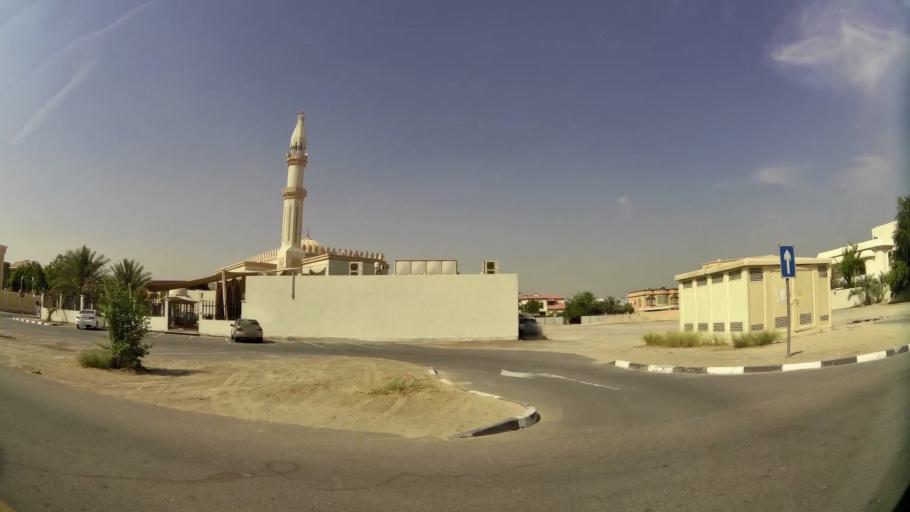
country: AE
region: Ash Shariqah
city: Sharjah
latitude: 25.2726
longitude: 55.4092
